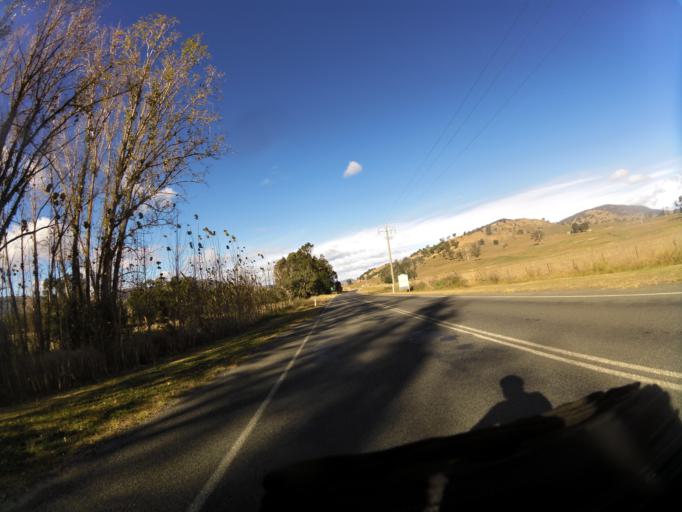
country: AU
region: New South Wales
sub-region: Greater Hume Shire
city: Holbrook
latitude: -35.9639
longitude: 147.7391
